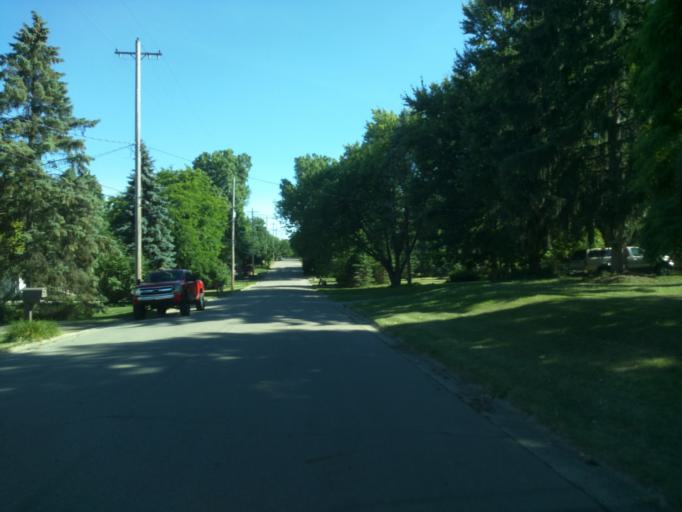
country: US
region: Michigan
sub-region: Eaton County
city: Waverly
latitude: 42.7446
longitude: -84.6361
